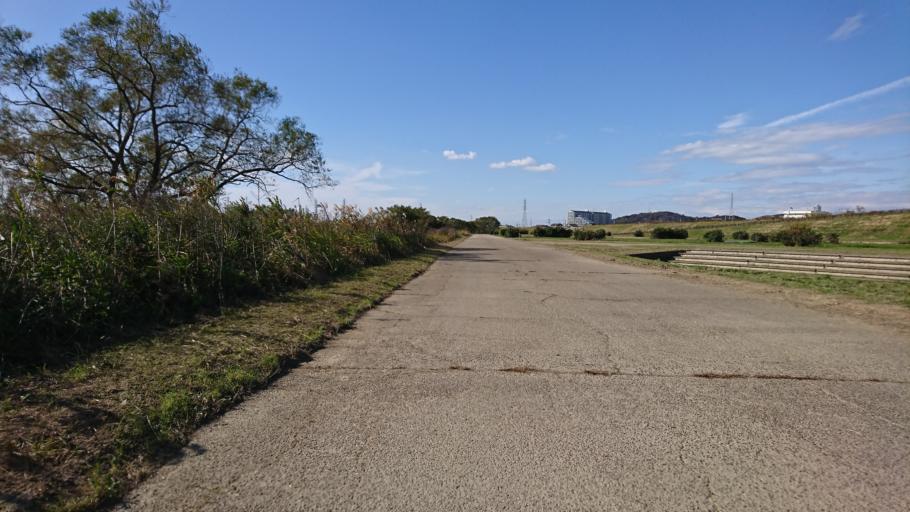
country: JP
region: Hyogo
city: Kakogawacho-honmachi
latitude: 34.7725
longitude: 134.8203
